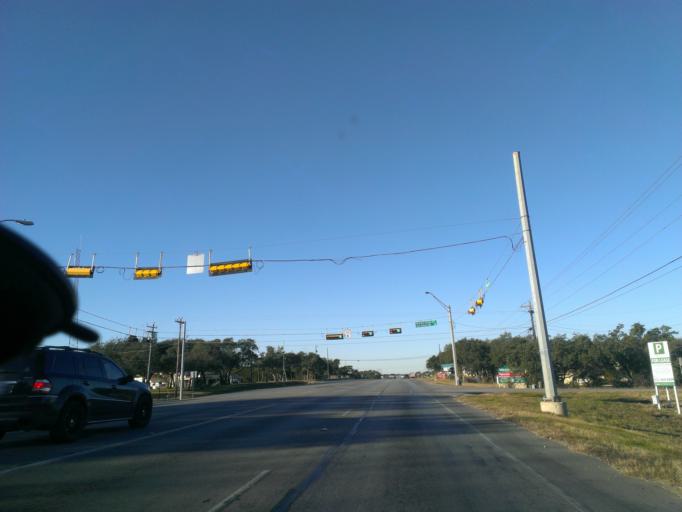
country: US
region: Texas
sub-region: Travis County
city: Bee Cave
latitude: 30.2089
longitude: -97.9729
